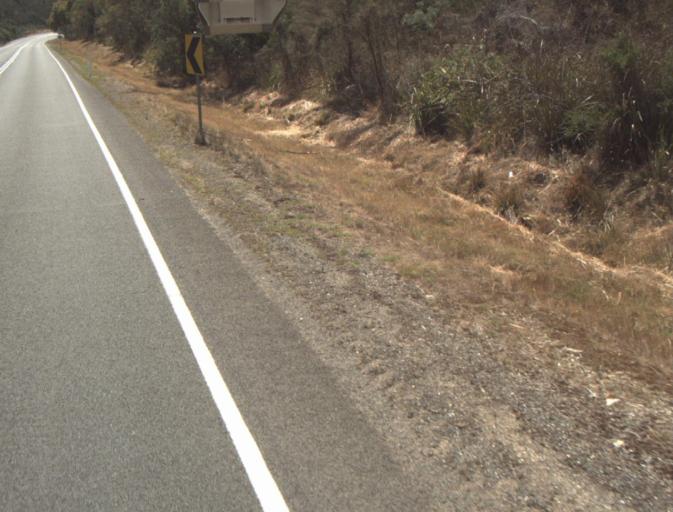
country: AU
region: Tasmania
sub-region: Launceston
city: Mayfield
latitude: -41.3631
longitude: 147.1448
